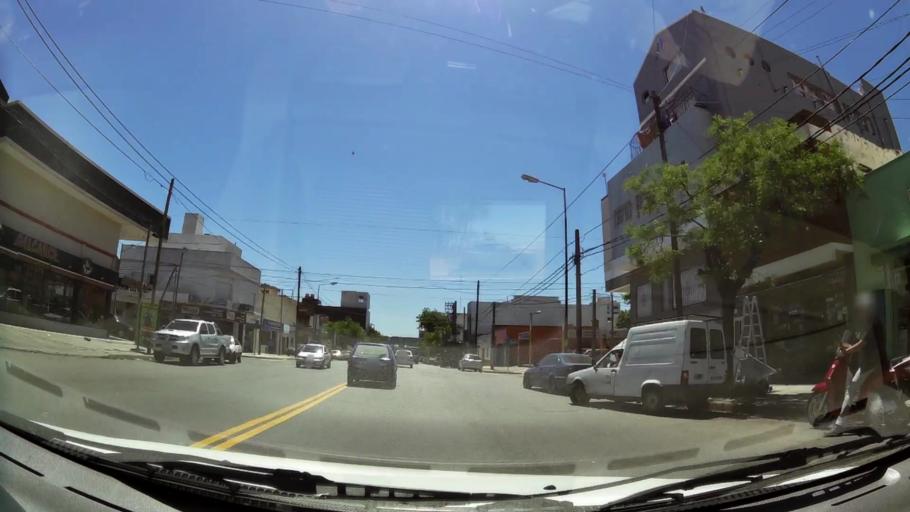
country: AR
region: Buenos Aires
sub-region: Partido de General San Martin
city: General San Martin
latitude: -34.5748
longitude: -58.5464
